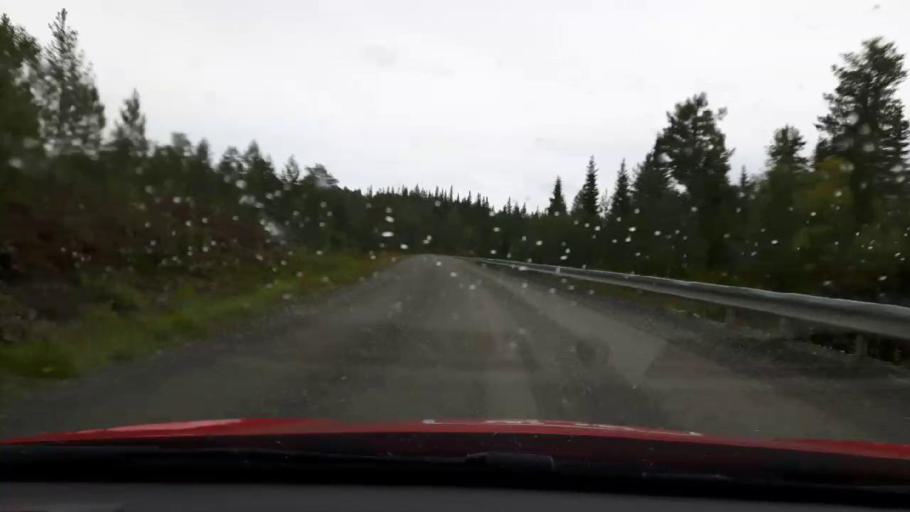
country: NO
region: Nord-Trondelag
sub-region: Meraker
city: Meraker
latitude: 63.6464
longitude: 12.2640
